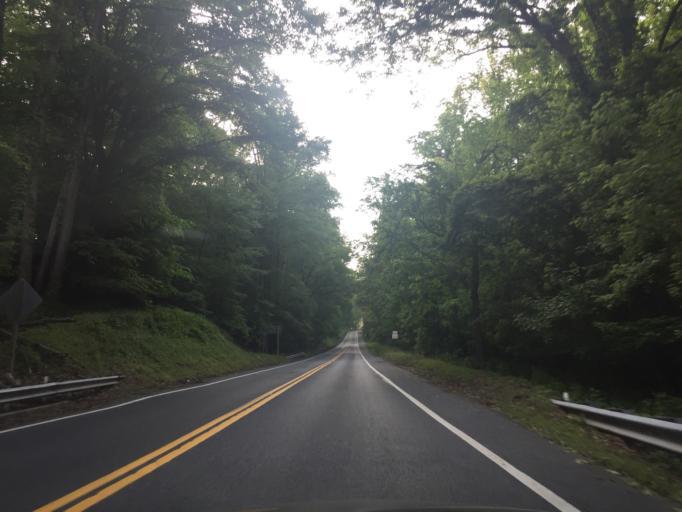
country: US
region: Maryland
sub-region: Frederick County
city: Point of Rocks
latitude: 39.2870
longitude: -77.5318
